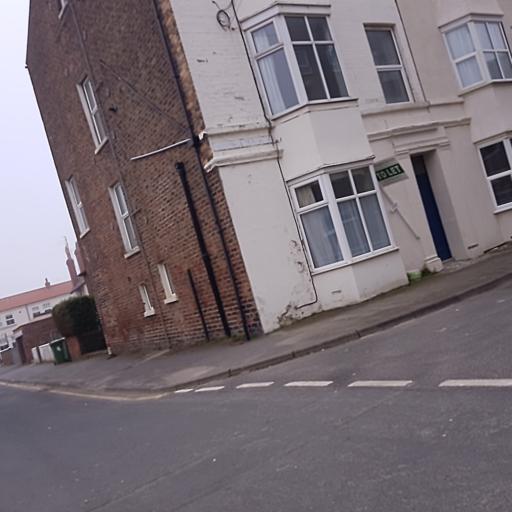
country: GB
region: England
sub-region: North Yorkshire
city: Filey
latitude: 54.2054
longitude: -0.2876
